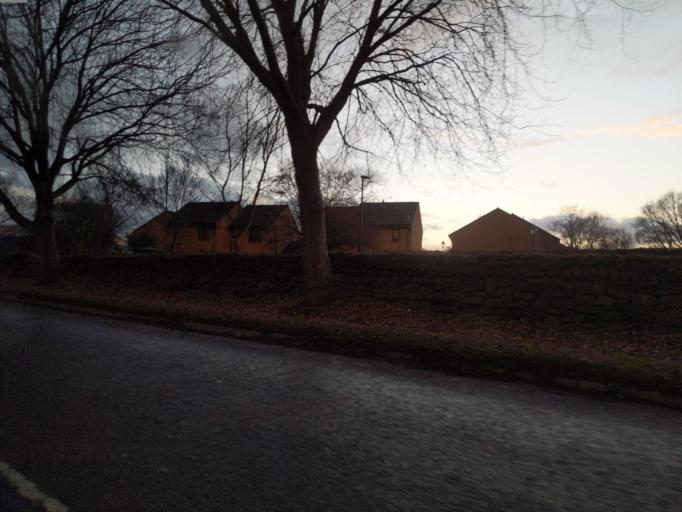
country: GB
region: England
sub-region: Devon
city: Barnstaple
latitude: 51.0682
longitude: -4.0858
